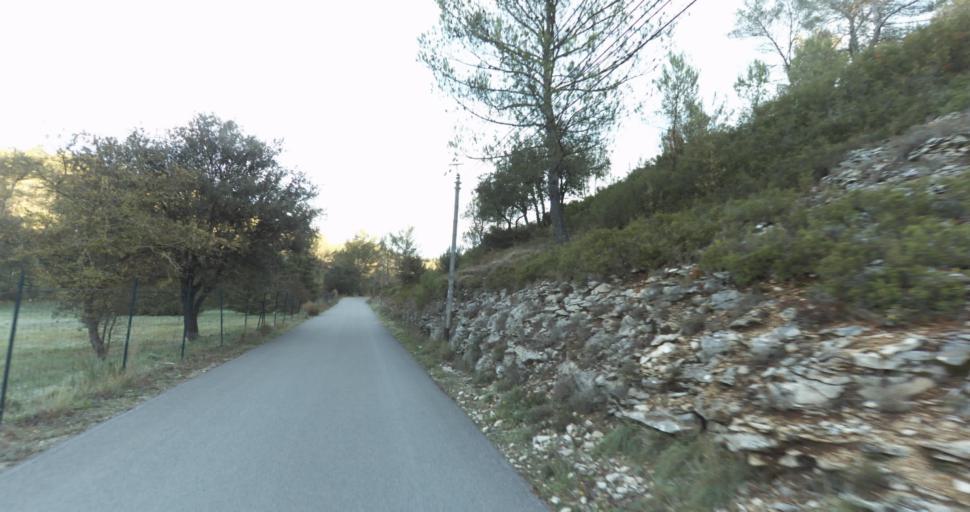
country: FR
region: Provence-Alpes-Cote d'Azur
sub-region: Departement des Bouches-du-Rhone
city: Venelles
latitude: 43.5861
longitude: 5.5072
